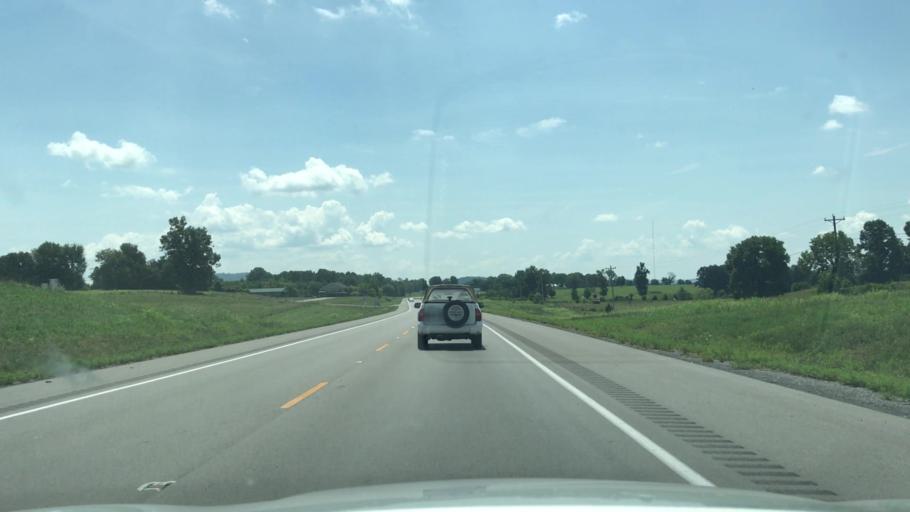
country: US
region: Tennessee
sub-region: Pickett County
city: Byrdstown
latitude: 36.6325
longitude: -85.0958
